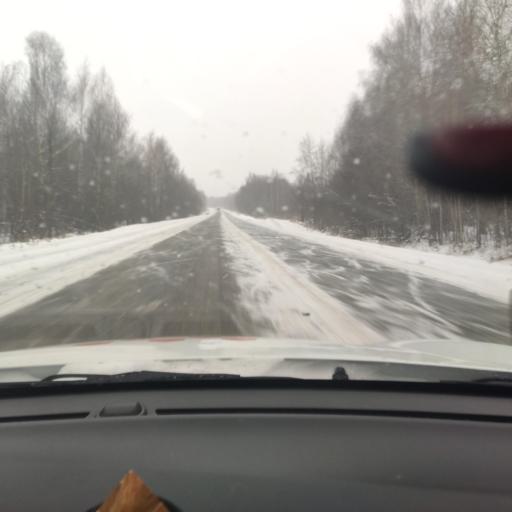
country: RU
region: Tatarstan
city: Verkhniy Uslon
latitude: 55.6948
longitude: 48.8805
